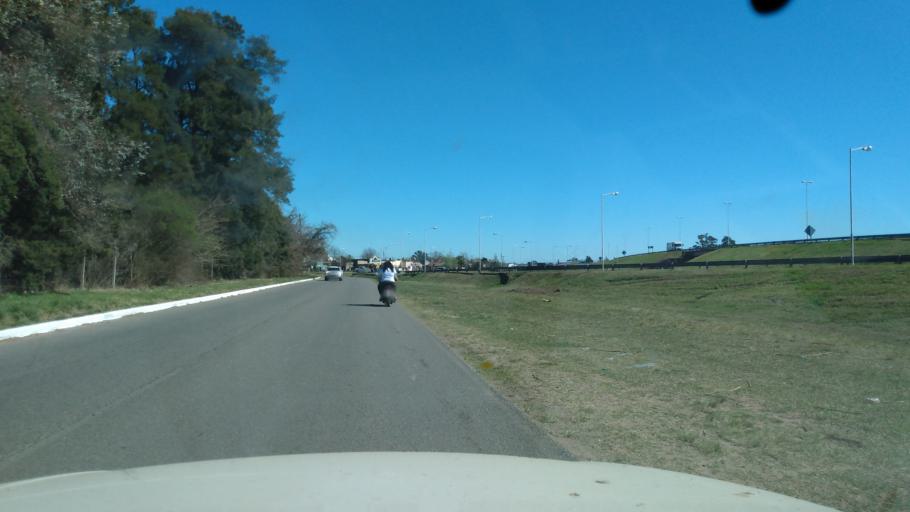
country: AR
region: Buenos Aires
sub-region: Partido de Lujan
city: Lujan
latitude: -34.5573
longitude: -59.0986
